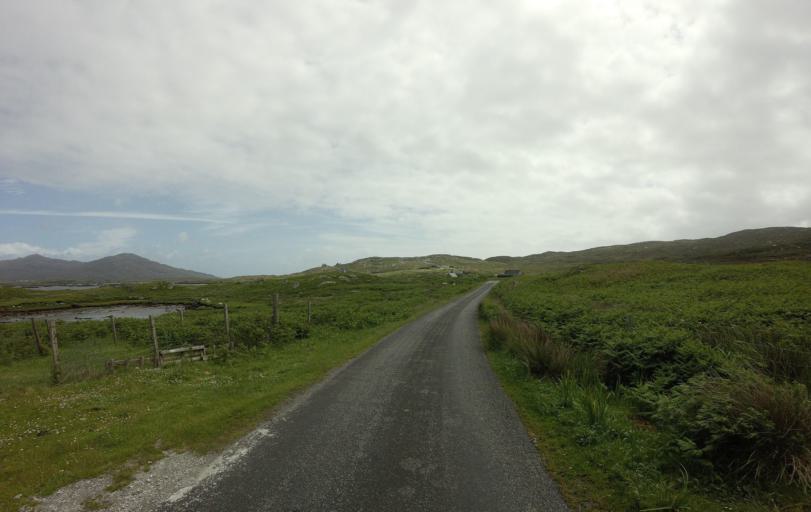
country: GB
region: Scotland
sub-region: Eilean Siar
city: Isle of South Uist
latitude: 57.1367
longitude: -7.3379
